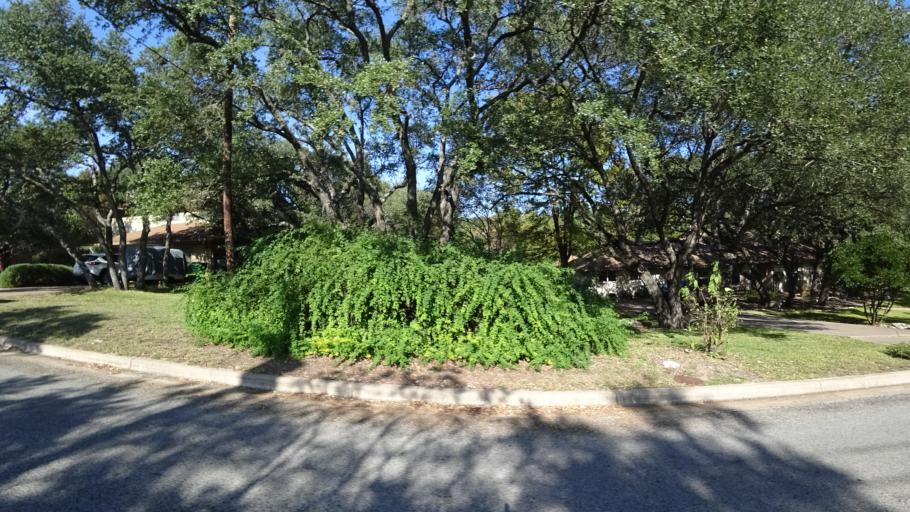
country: US
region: Texas
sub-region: Travis County
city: Shady Hollow
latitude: 30.2220
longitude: -97.9099
